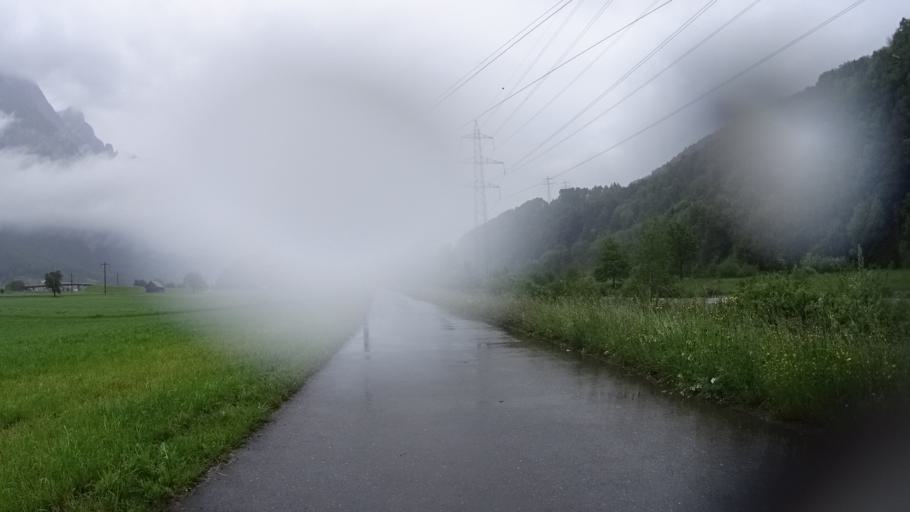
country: CH
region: Saint Gallen
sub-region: Wahlkreis Sarganserland
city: Flums
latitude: 47.0679
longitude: 9.3804
